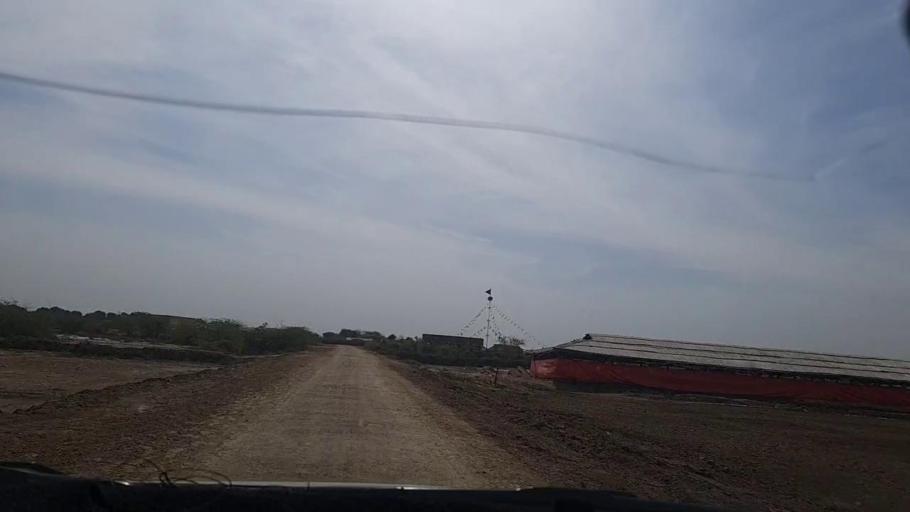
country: PK
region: Sindh
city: Dhoro Naro
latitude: 25.4369
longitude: 69.4974
